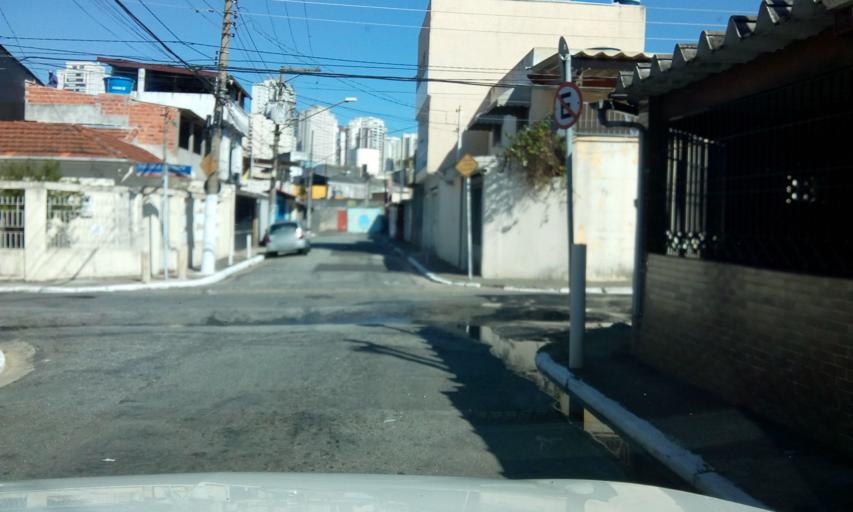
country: BR
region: Sao Paulo
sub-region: Guarulhos
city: Guarulhos
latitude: -23.5372
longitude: -46.5553
